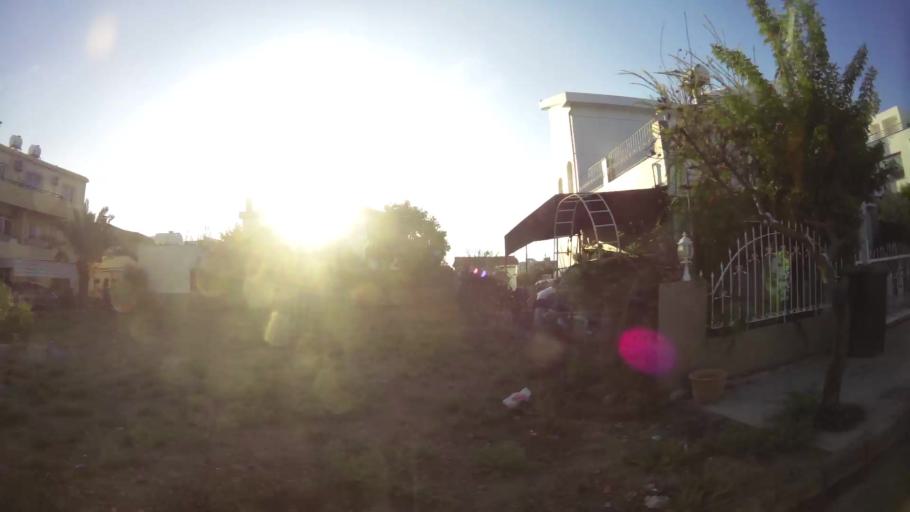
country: CY
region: Lefkosia
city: Nicosia
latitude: 35.1930
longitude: 33.3250
